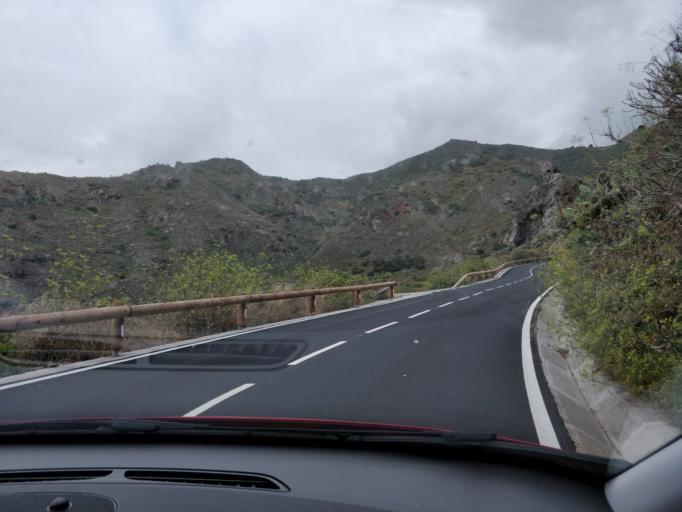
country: ES
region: Canary Islands
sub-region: Provincia de Santa Cruz de Tenerife
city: Tanque
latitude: 28.3494
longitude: -16.8449
